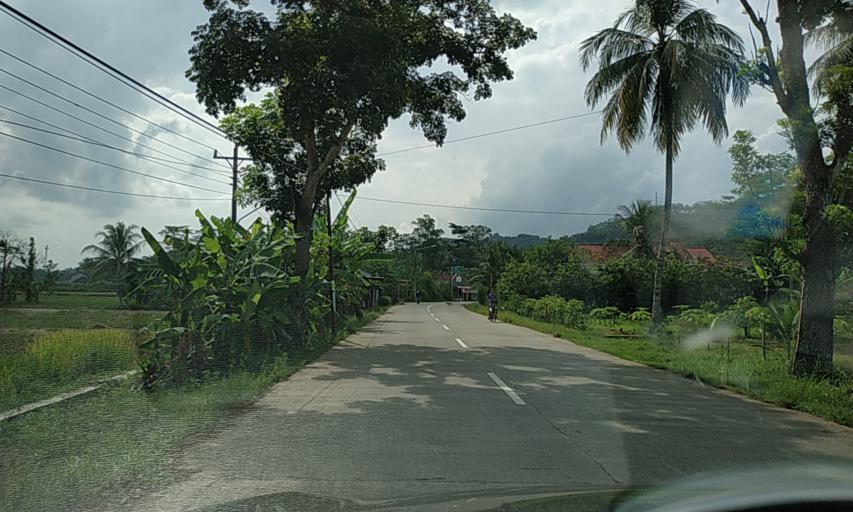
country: ID
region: Central Java
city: Winangun
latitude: -7.3437
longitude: 108.7080
